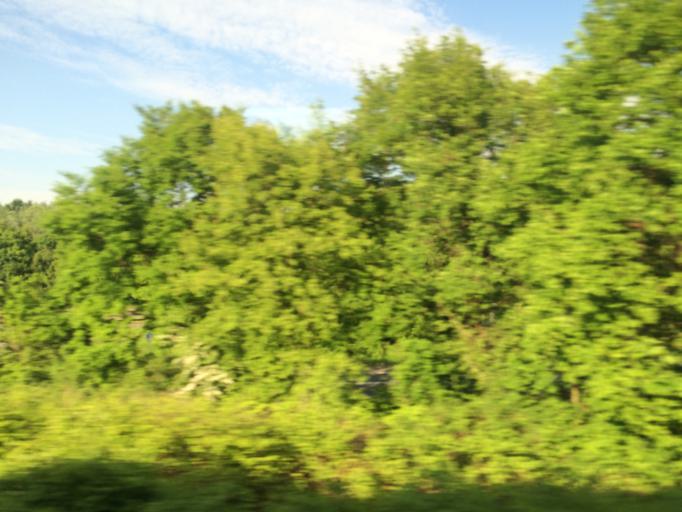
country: DE
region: North Rhine-Westphalia
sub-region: Regierungsbezirk Dusseldorf
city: Hilden
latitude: 51.1521
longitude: 6.8894
